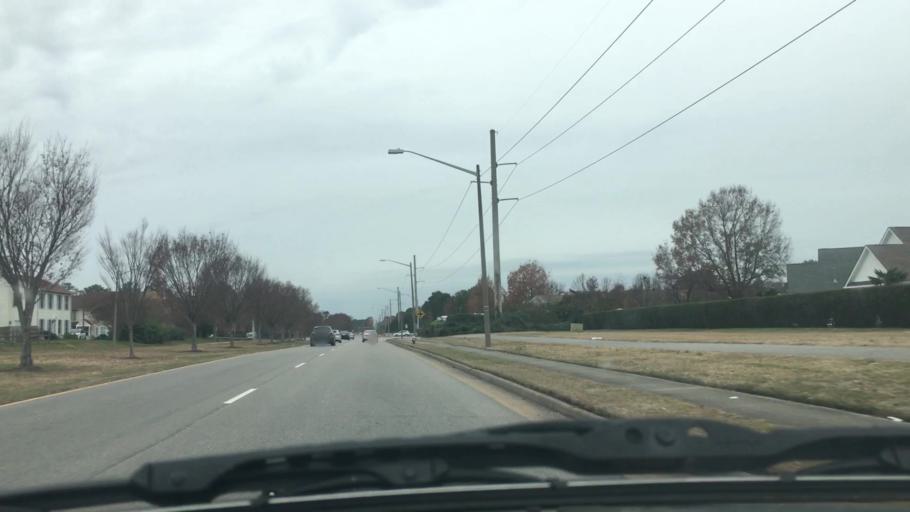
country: US
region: Virginia
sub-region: City of Virginia Beach
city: Virginia Beach
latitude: 36.8074
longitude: -76.1182
